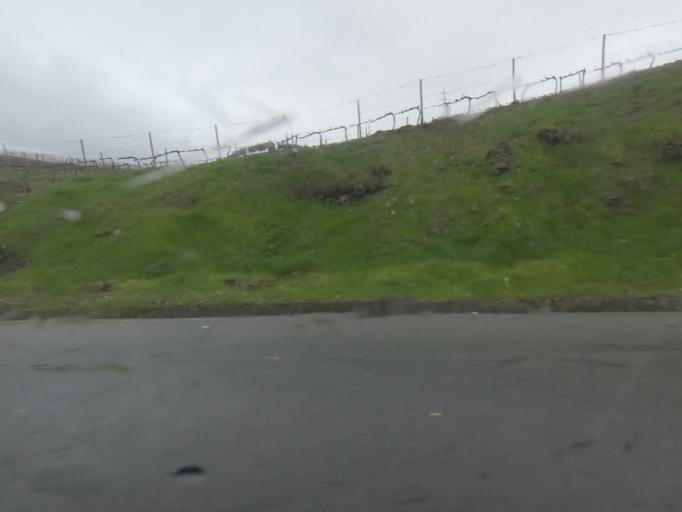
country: PT
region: Vila Real
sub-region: Peso da Regua
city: Peso da Regua
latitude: 41.1714
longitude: -7.7606
